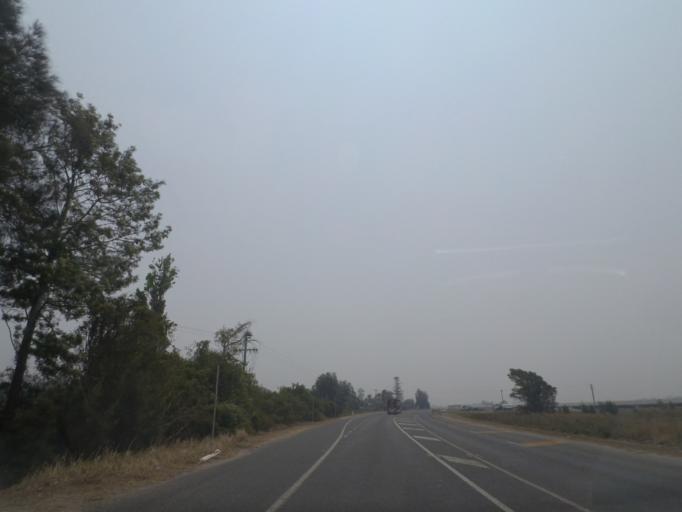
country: AU
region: New South Wales
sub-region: Clarence Valley
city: Maclean
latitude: -29.4207
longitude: 153.2407
